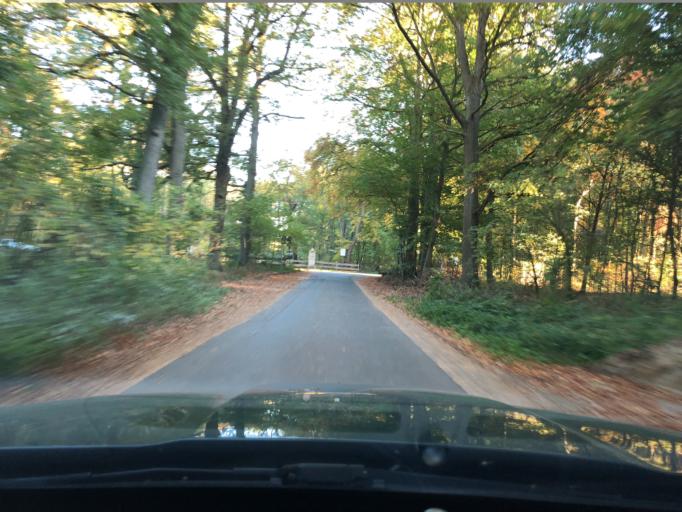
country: DE
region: North Rhine-Westphalia
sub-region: Regierungsbezirk Munster
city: Telgte
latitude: 52.0178
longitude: 7.7037
